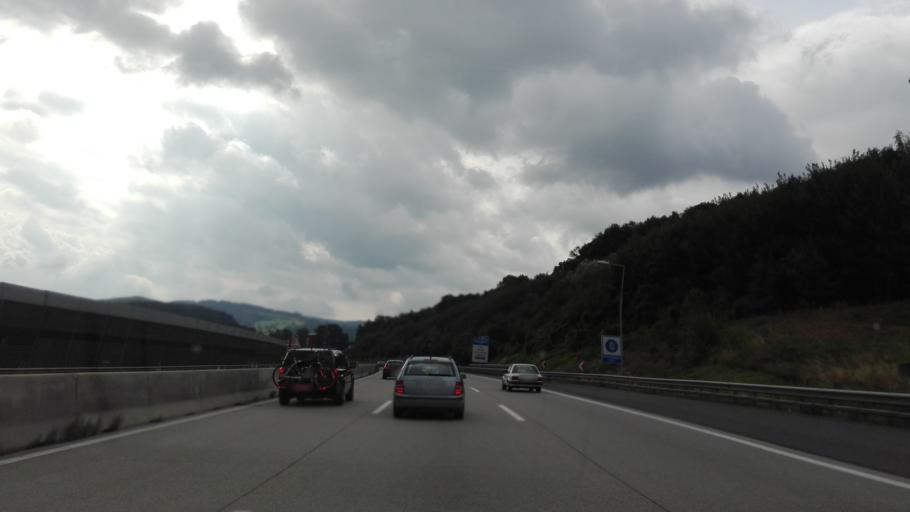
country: AT
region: Lower Austria
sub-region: Politischer Bezirk Sankt Polten
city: Altlengbach
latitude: 48.1568
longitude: 15.8918
